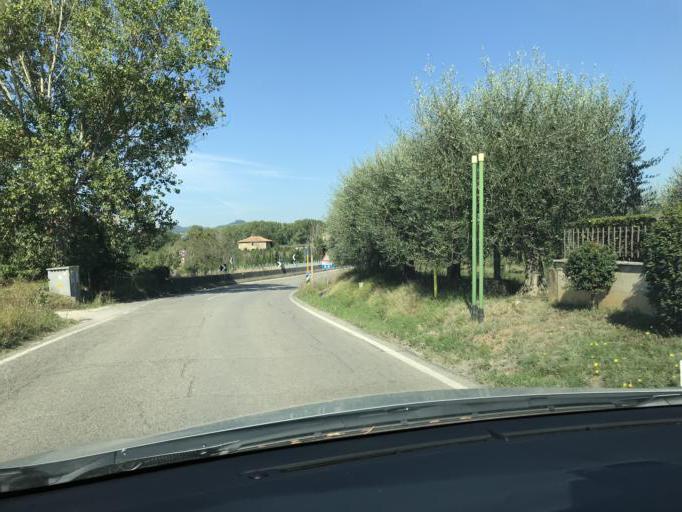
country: IT
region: Umbria
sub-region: Provincia di Perugia
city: Via Lippia
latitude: 43.1049
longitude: 12.4775
